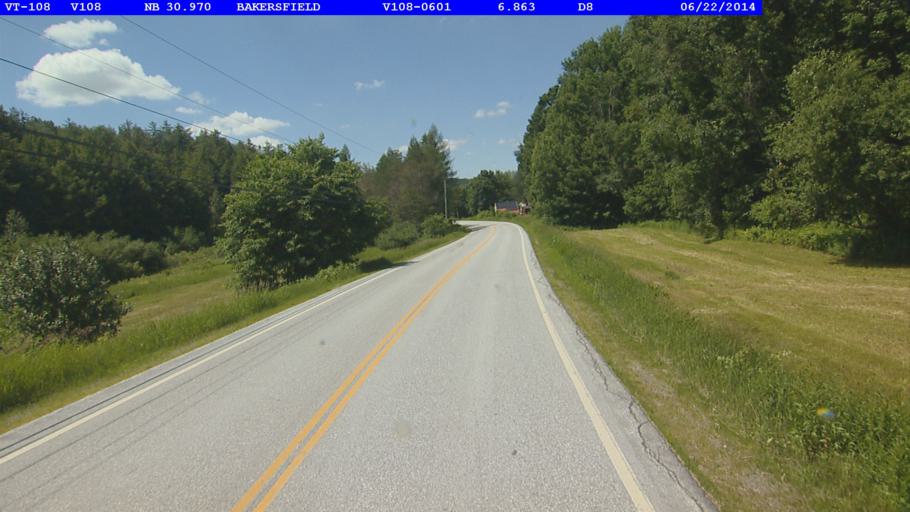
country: US
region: Vermont
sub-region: Franklin County
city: Enosburg Falls
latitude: 44.8237
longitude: -72.7961
